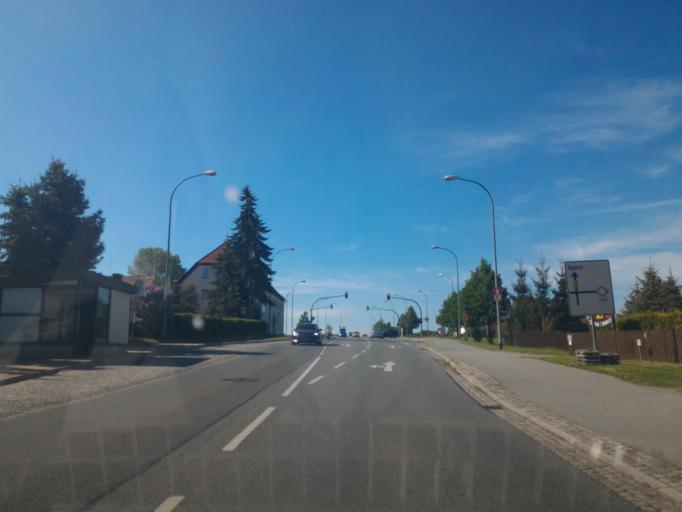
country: DE
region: Saxony
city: Neugersdorf
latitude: 51.0040
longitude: 14.6188
